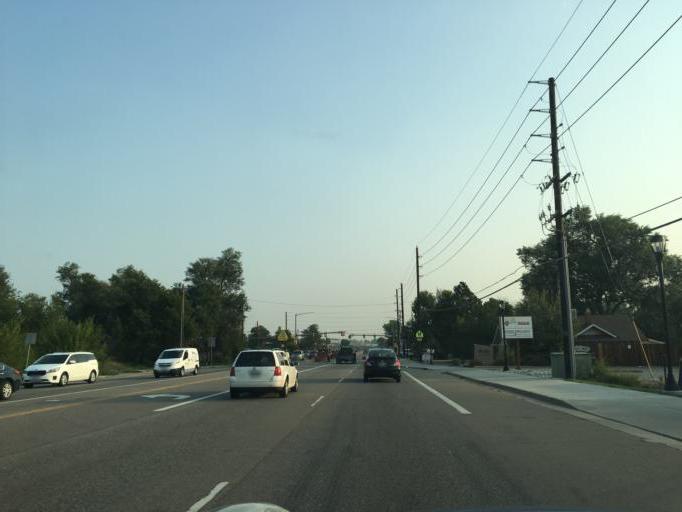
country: US
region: Colorado
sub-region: Jefferson County
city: Wheat Ridge
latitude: 39.7764
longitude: -105.1096
